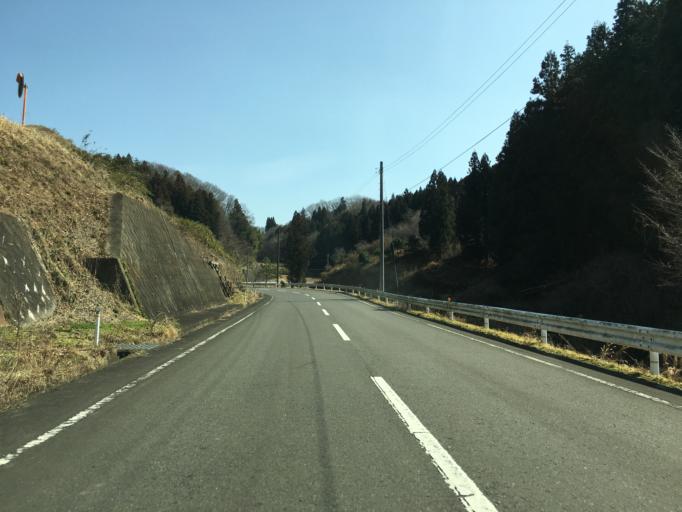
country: JP
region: Fukushima
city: Ishikawa
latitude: 37.1038
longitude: 140.4352
